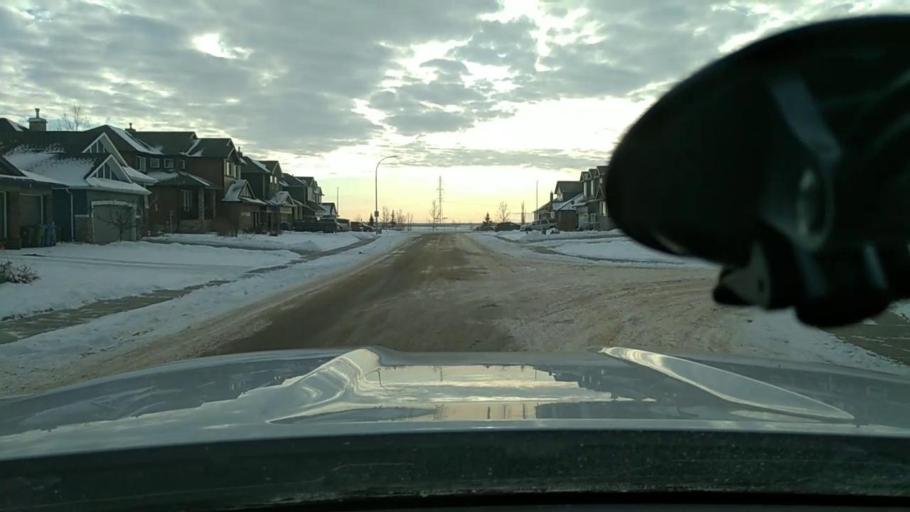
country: CA
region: Alberta
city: Chestermere
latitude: 50.9619
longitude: -113.6621
